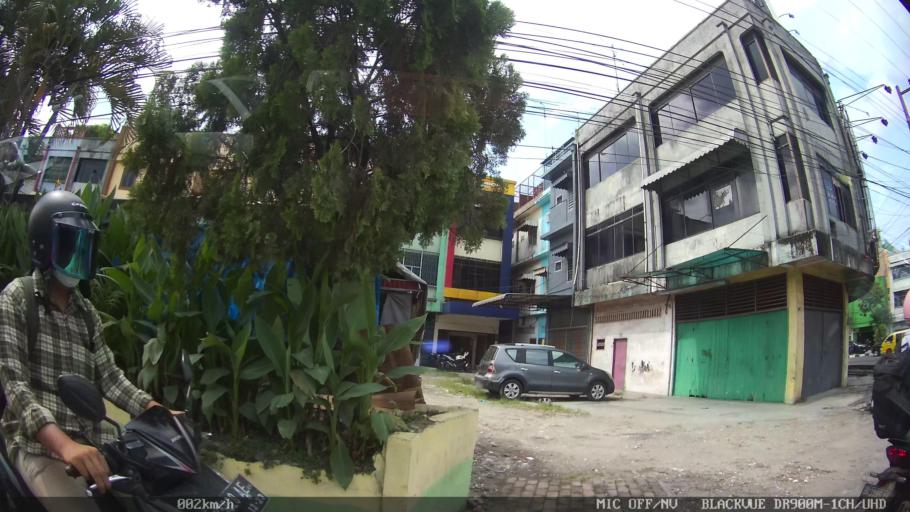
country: ID
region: North Sumatra
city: Medan
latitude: 3.5726
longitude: 98.6851
